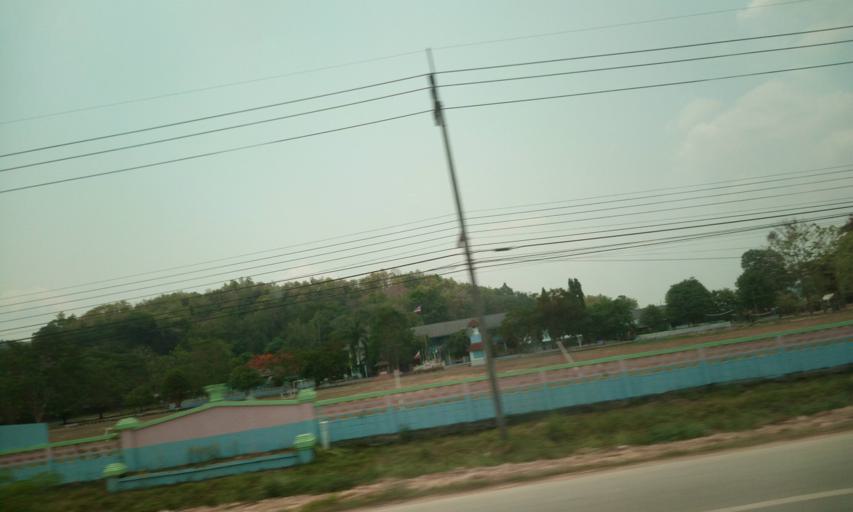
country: TH
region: Chiang Rai
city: Thoeng
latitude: 19.6889
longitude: 100.1417
